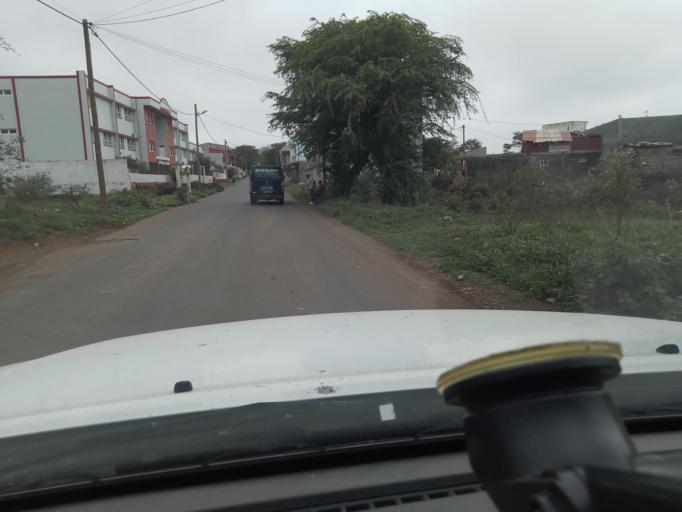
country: CV
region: Santa Catarina
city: Assomada
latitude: 15.1277
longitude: -23.6731
